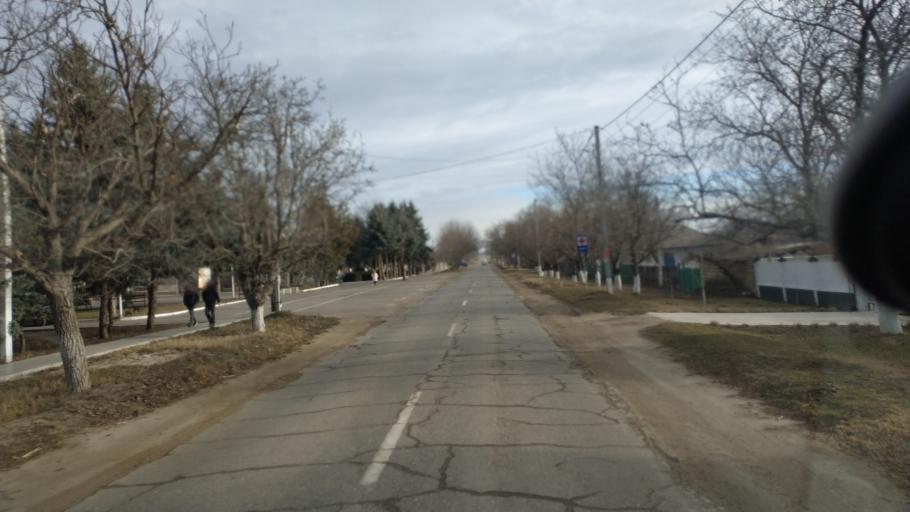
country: MD
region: Criuleni
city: Criuleni
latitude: 47.1660
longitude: 29.1225
